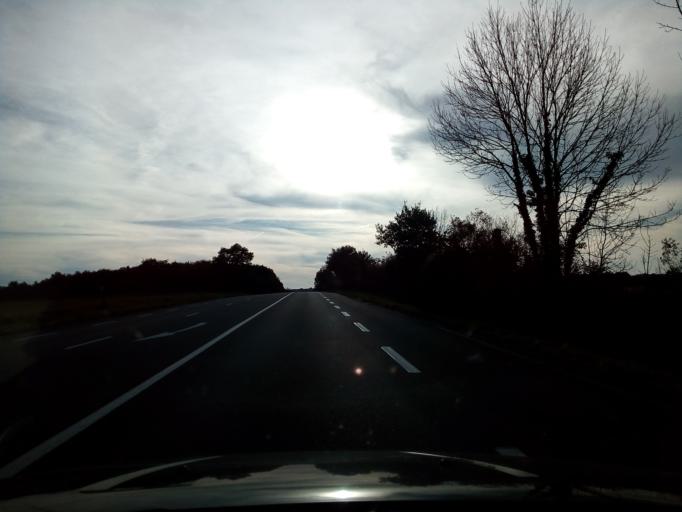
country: FR
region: Poitou-Charentes
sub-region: Departement de la Charente
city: Saint-Claud
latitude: 45.9235
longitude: 0.5181
